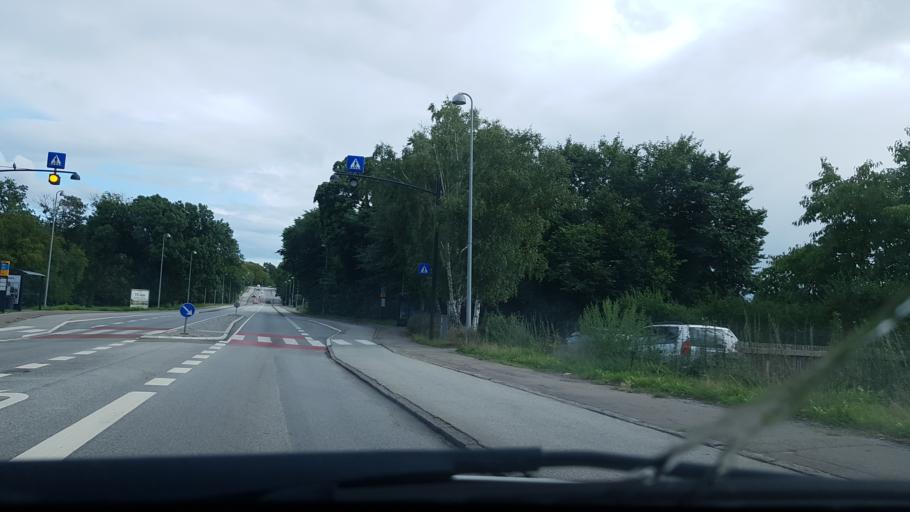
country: DK
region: Capital Region
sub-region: Horsholm Kommune
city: Horsholm
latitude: 55.8952
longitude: 12.4907
